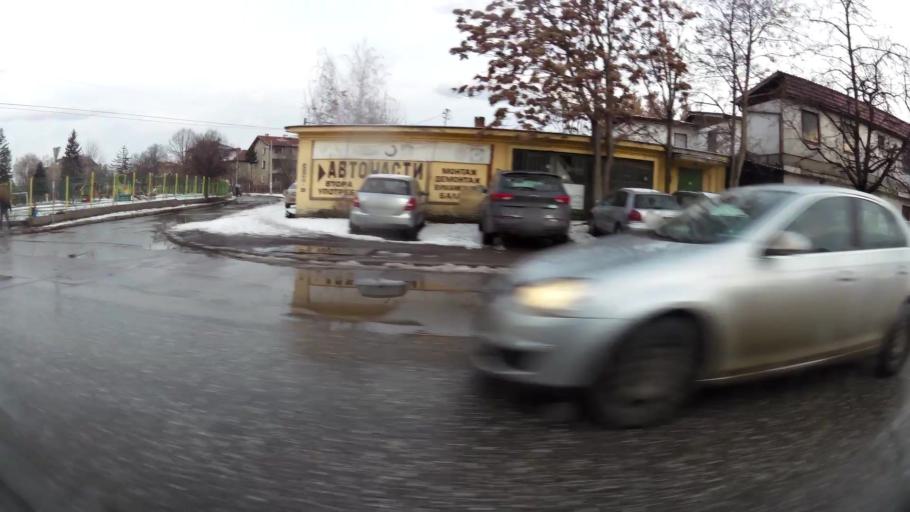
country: BG
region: Sofia-Capital
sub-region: Stolichna Obshtina
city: Sofia
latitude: 42.7201
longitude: 23.3437
